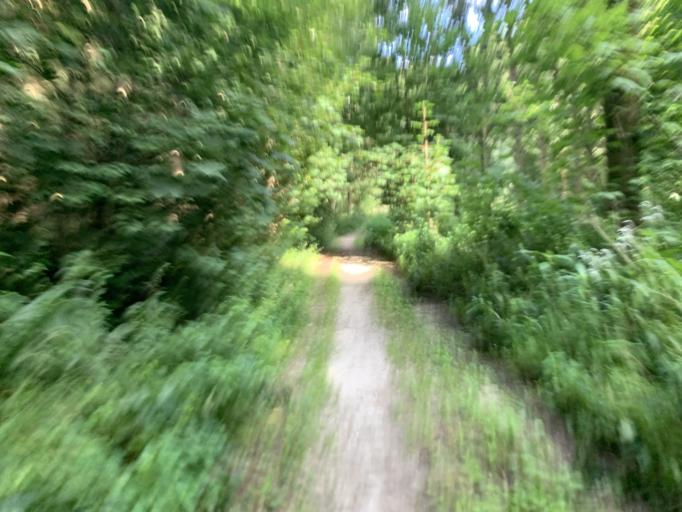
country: DE
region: Bavaria
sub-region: Upper Bavaria
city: Freising
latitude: 48.4217
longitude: 11.7379
